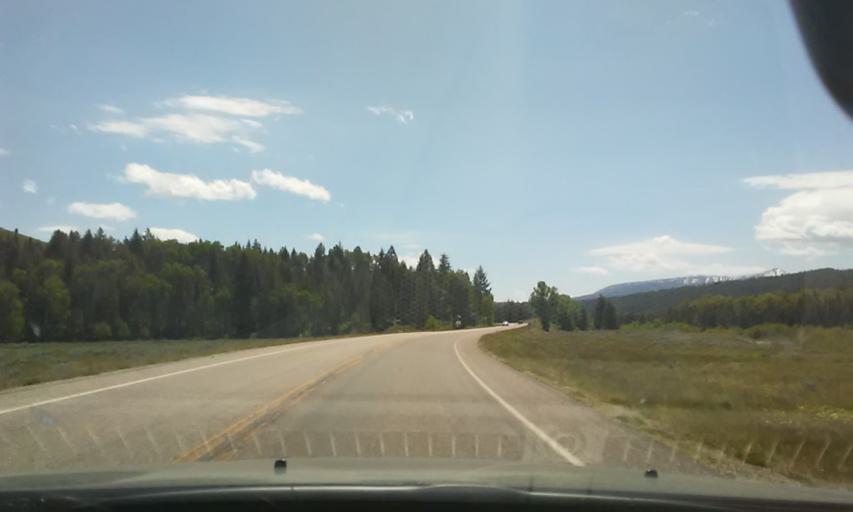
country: US
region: Wyoming
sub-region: Teton County
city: Jackson
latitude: 43.8398
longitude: -110.5053
